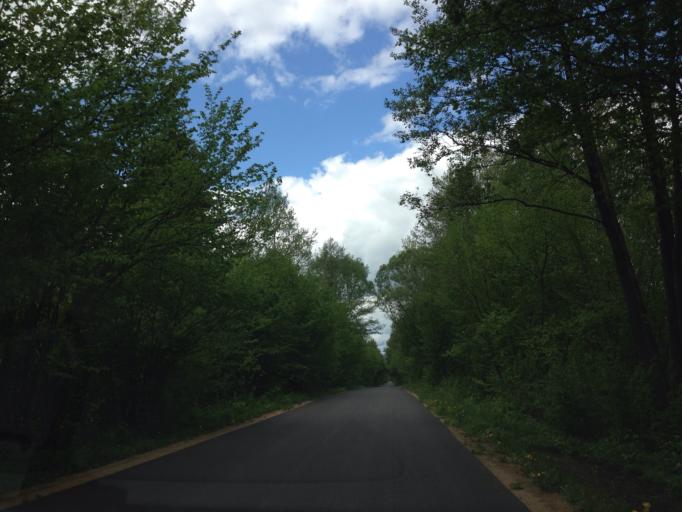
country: PL
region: Podlasie
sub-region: Powiat grajewski
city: Radzilow
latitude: 53.3254
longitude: 22.6008
